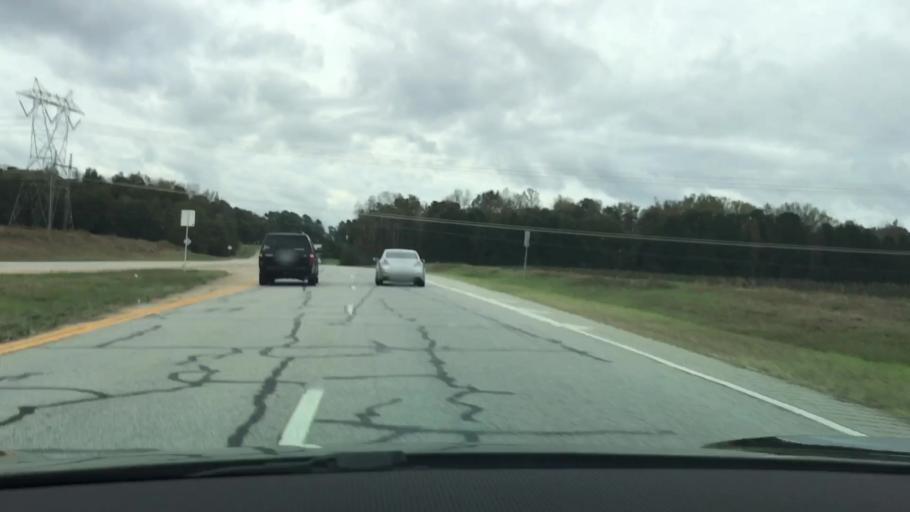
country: US
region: Georgia
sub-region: Jefferson County
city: Wadley
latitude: 32.8898
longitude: -82.4001
